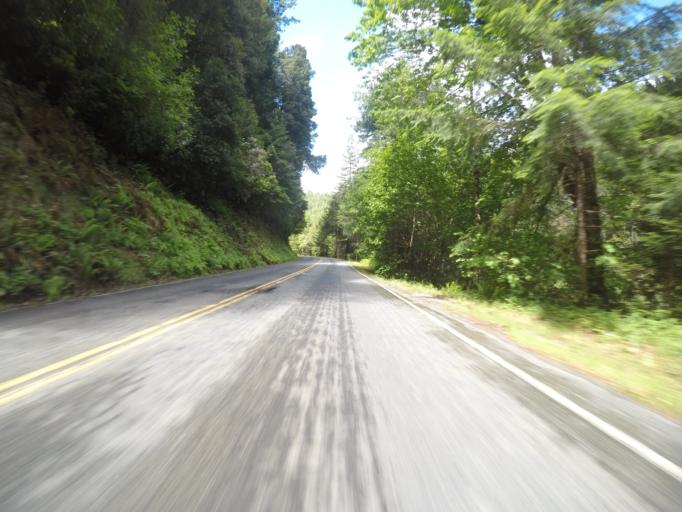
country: US
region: California
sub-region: Del Norte County
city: Bertsch-Oceanview
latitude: 41.7953
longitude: -124.0425
